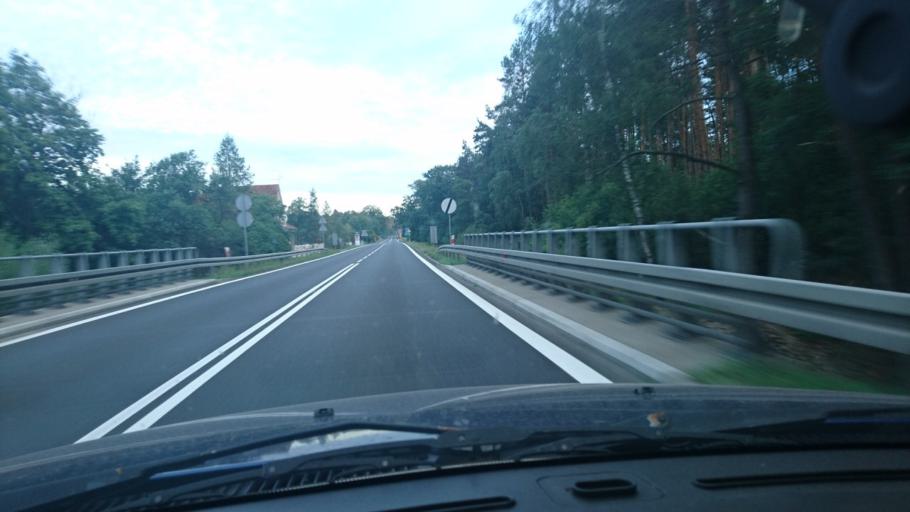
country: PL
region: Silesian Voivodeship
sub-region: Powiat tarnogorski
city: Tworog
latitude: 50.5894
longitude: 18.7023
